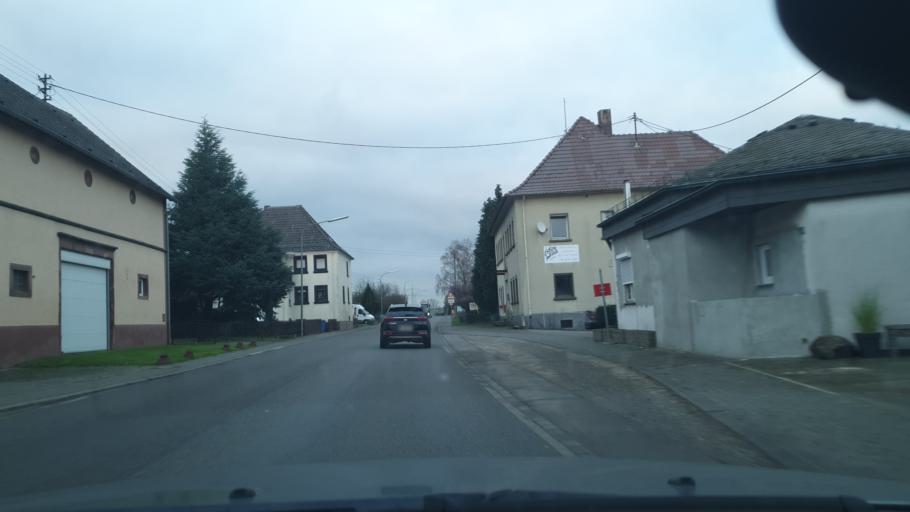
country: DE
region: Rheinland-Pfalz
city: Grossbundenbach
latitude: 49.3015
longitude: 7.3924
